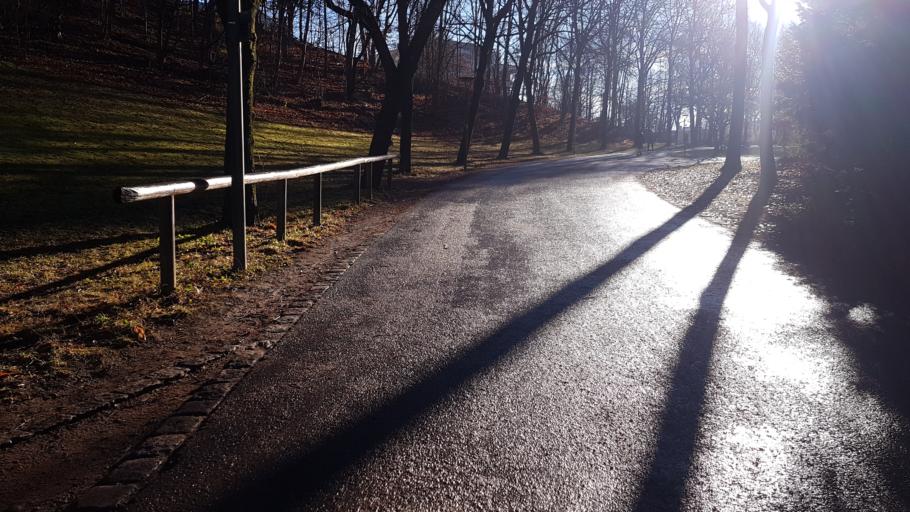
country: DE
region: Bavaria
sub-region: Upper Bavaria
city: Munich
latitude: 48.1238
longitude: 11.5308
